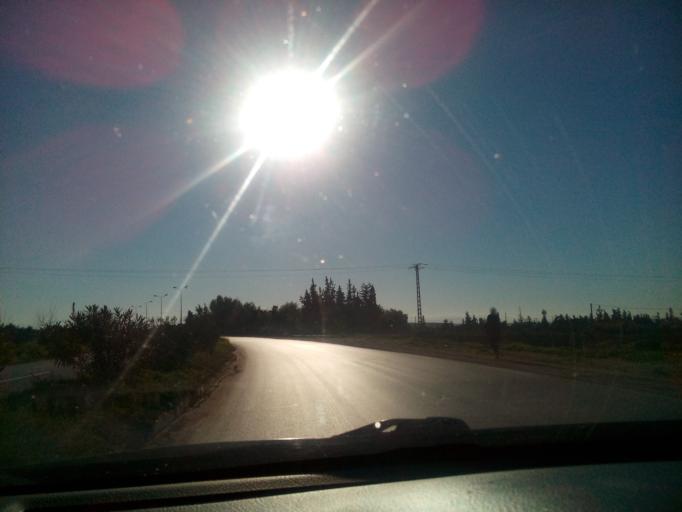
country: DZ
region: Relizane
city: Relizane
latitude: 35.7208
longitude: 0.5766
